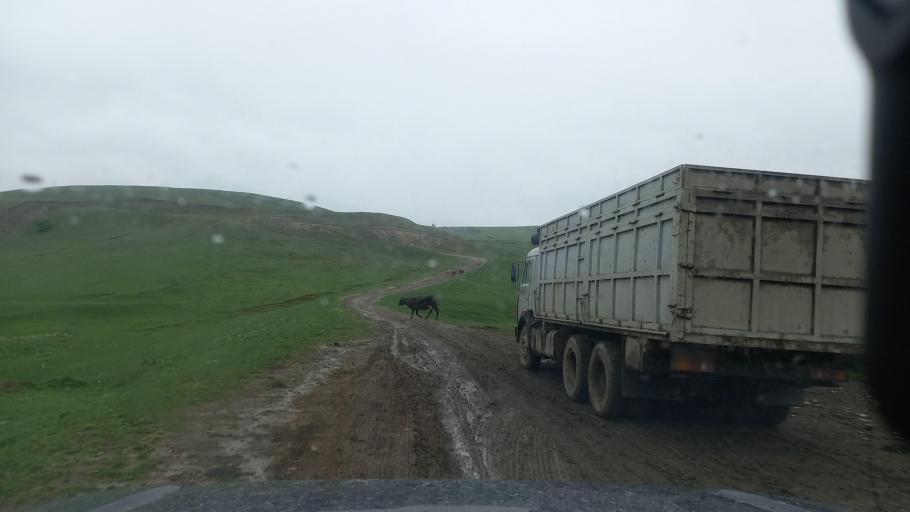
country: RU
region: Kabardino-Balkariya
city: Kamennomostskoye
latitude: 43.6982
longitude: 43.0117
